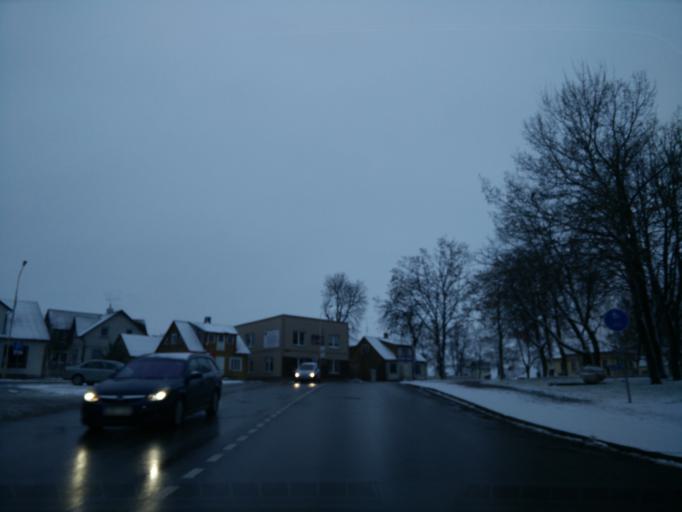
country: LT
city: Kelme
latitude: 55.6300
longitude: 22.9347
